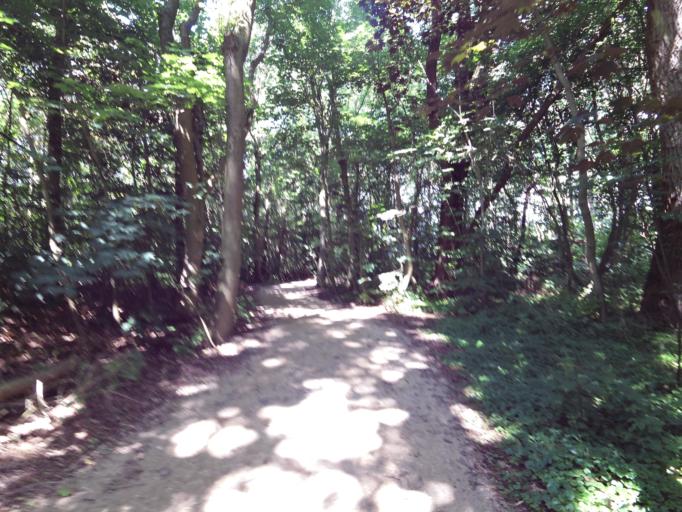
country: NL
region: Zeeland
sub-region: Gemeente Sluis
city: Sluis
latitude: 51.3591
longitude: 3.3457
